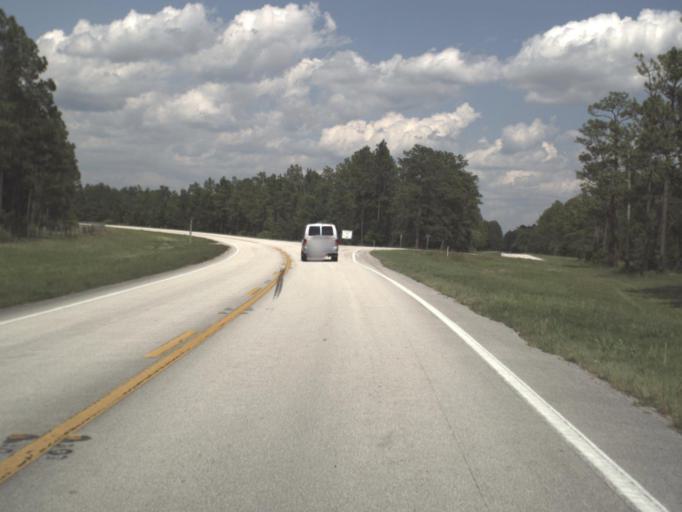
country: US
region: Florida
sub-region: Bradford County
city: Starke
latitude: 29.9385
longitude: -82.0226
